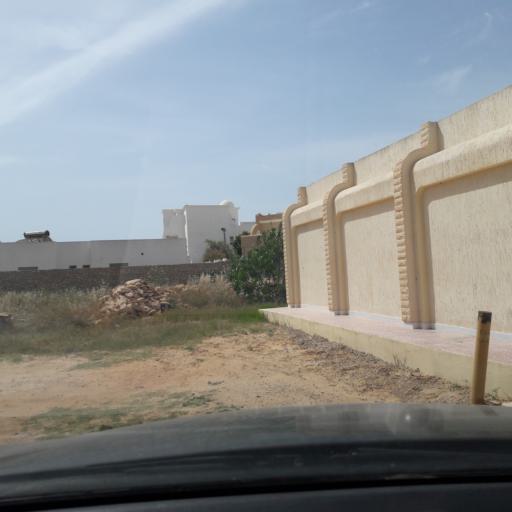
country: TN
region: Safaqis
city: Al Qarmadah
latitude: 34.7960
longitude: 10.7542
